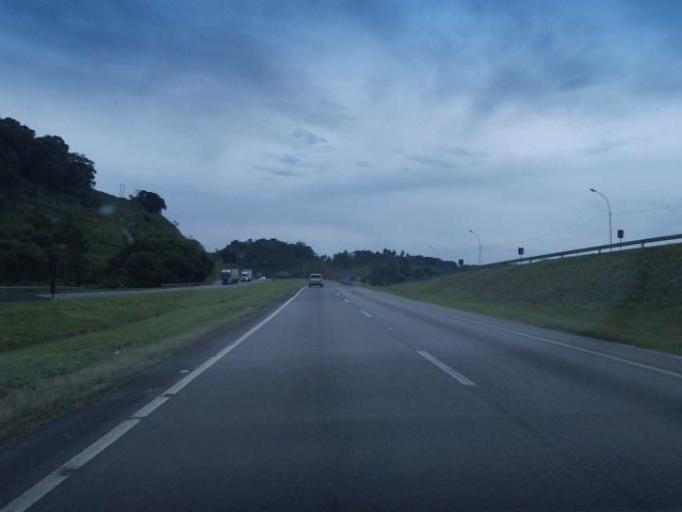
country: BR
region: Sao Paulo
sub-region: Juquia
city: Juquia
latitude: -24.3319
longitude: -47.6359
